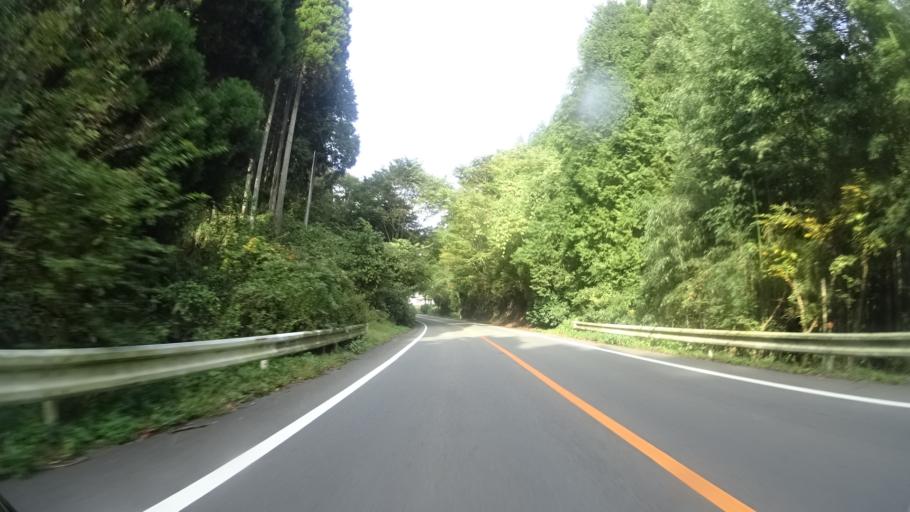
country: JP
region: Kumamoto
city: Aso
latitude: 33.0870
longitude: 131.0674
